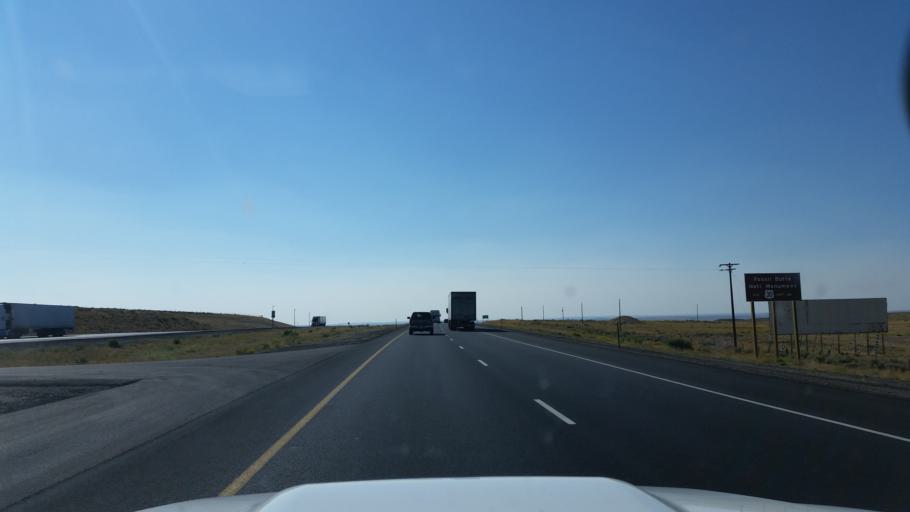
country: US
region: Wyoming
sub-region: Sweetwater County
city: Green River
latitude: 41.5425
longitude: -109.8930
